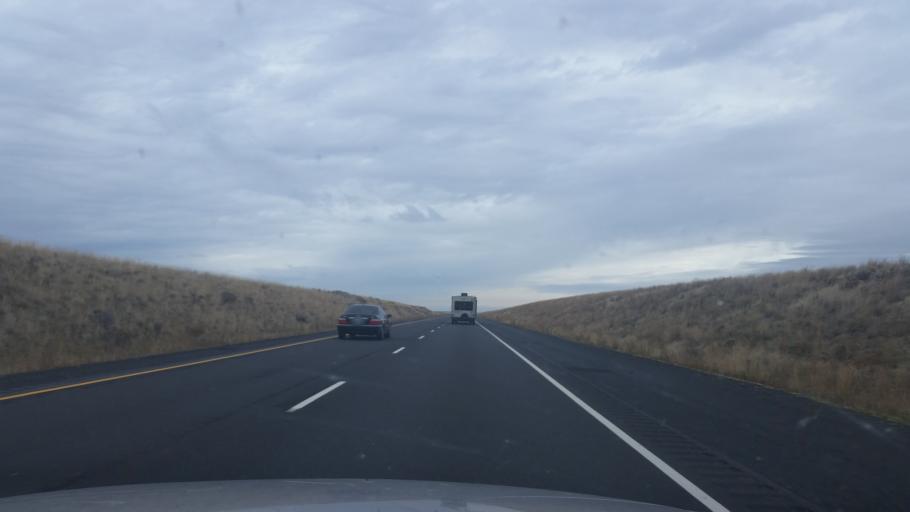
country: US
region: Washington
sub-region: Adams County
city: Ritzville
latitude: 47.0921
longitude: -118.6995
